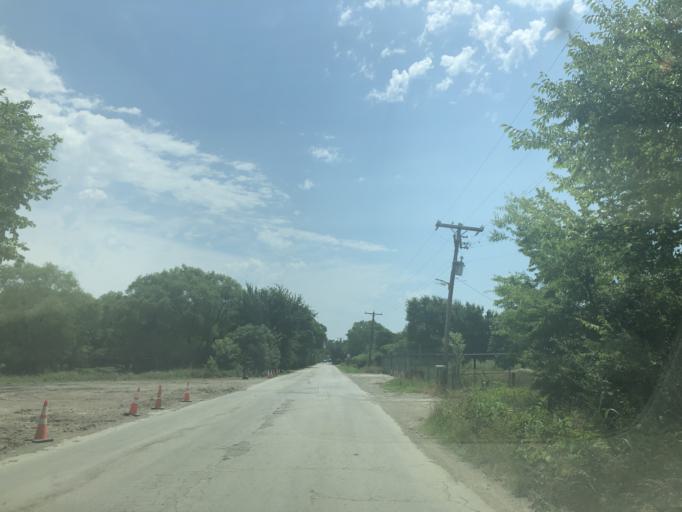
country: US
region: Texas
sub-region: Dallas County
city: Irving
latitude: 32.7866
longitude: -96.9517
